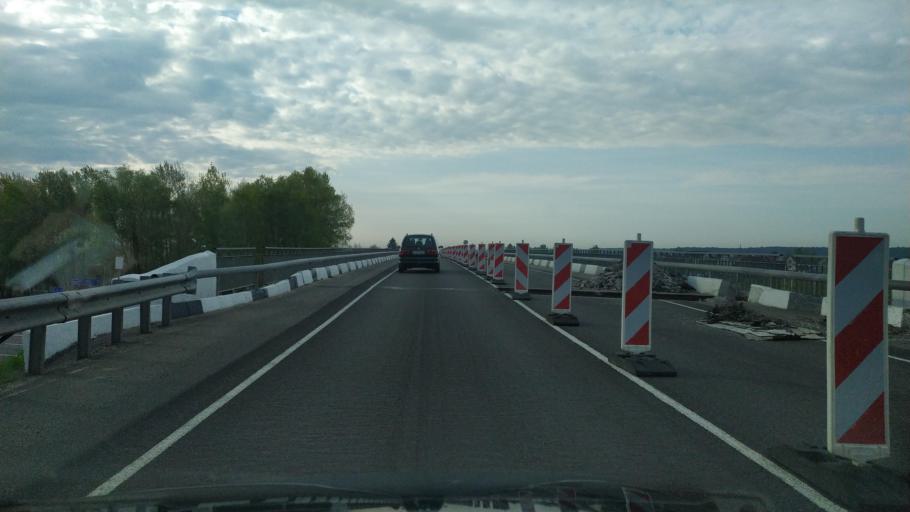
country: BY
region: Brest
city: Zhabinka
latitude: 52.1566
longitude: 24.0545
